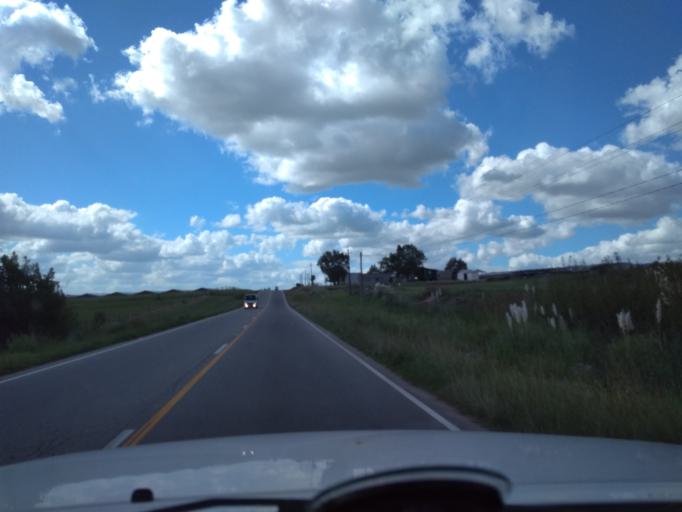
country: UY
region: Canelones
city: Joaquin Suarez
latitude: -34.7049
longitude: -56.0580
